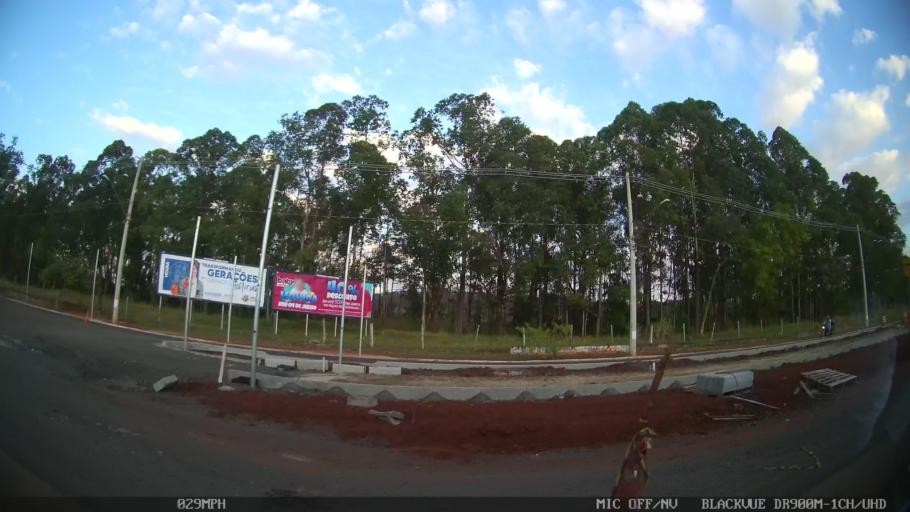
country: BR
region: Sao Paulo
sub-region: Ribeirao Preto
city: Ribeirao Preto
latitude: -21.1584
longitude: -47.7857
